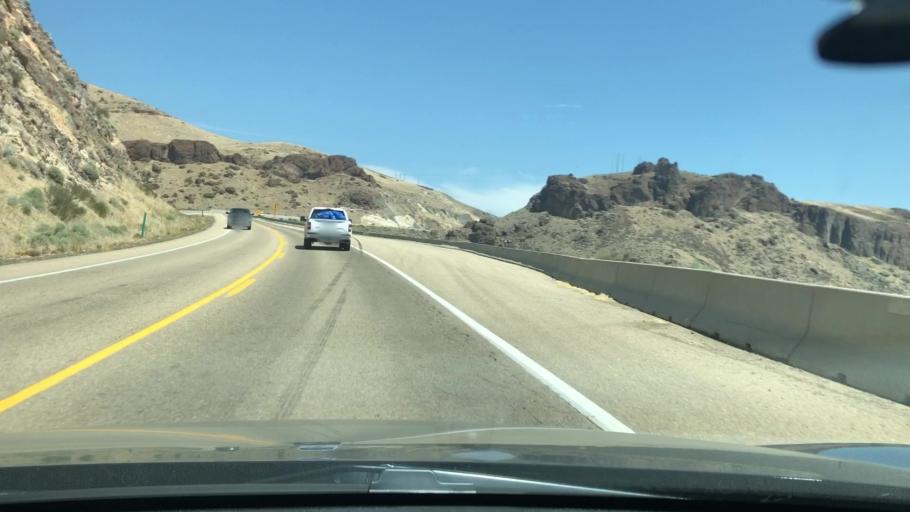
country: US
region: Idaho
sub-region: Owyhee County
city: Marsing
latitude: 43.4007
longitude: -116.8769
